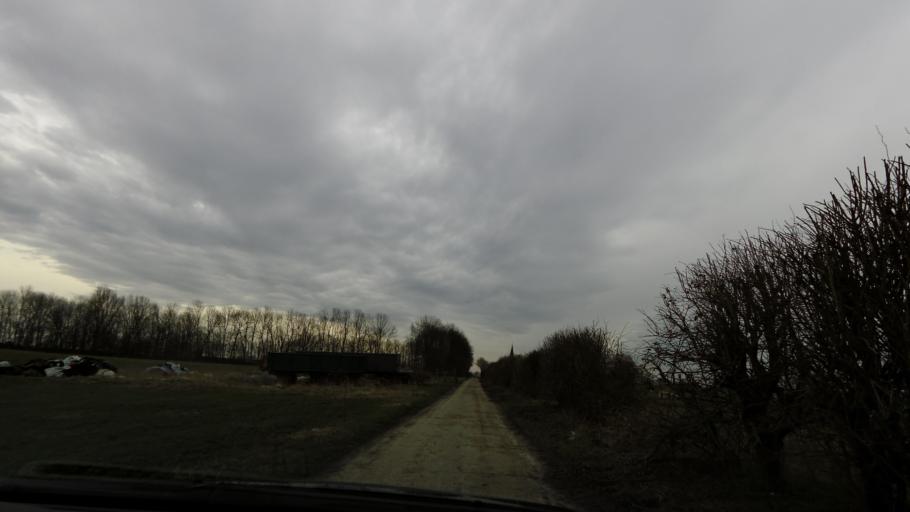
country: DE
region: North Rhine-Westphalia
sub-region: Regierungsbezirk Koln
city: Ubach-Palenberg
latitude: 50.9311
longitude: 6.0614
